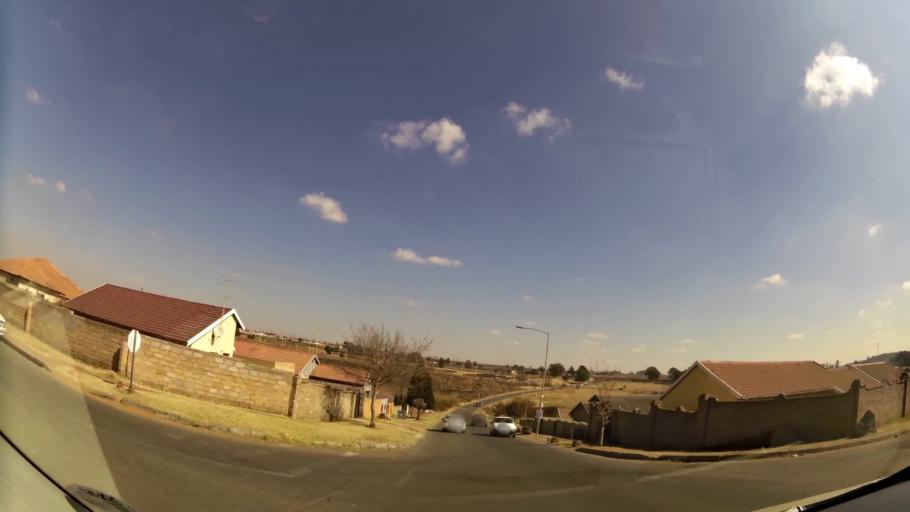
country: ZA
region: Gauteng
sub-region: West Rand District Municipality
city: Randfontein
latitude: -26.1558
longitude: 27.7660
